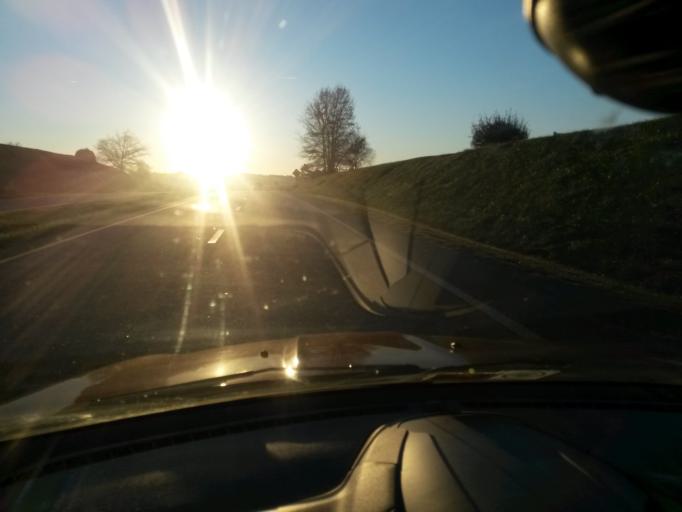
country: US
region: Virginia
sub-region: Franklin County
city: Rocky Mount
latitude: 37.0782
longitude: -79.9180
